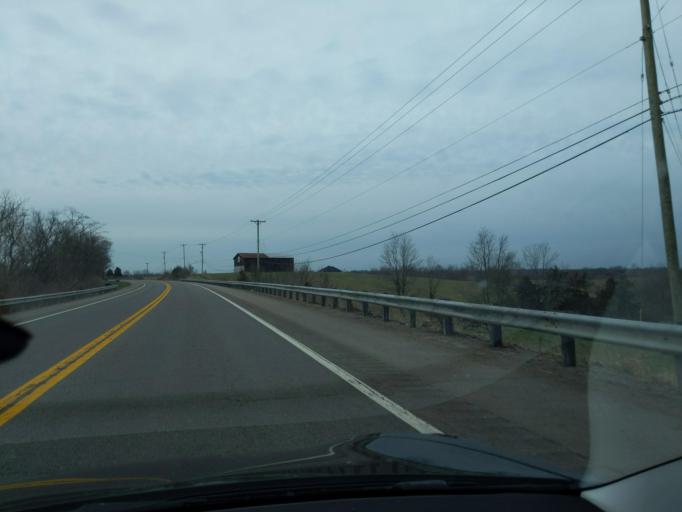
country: US
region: Kentucky
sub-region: Madison County
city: Richmond
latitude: 37.8731
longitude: -84.3013
